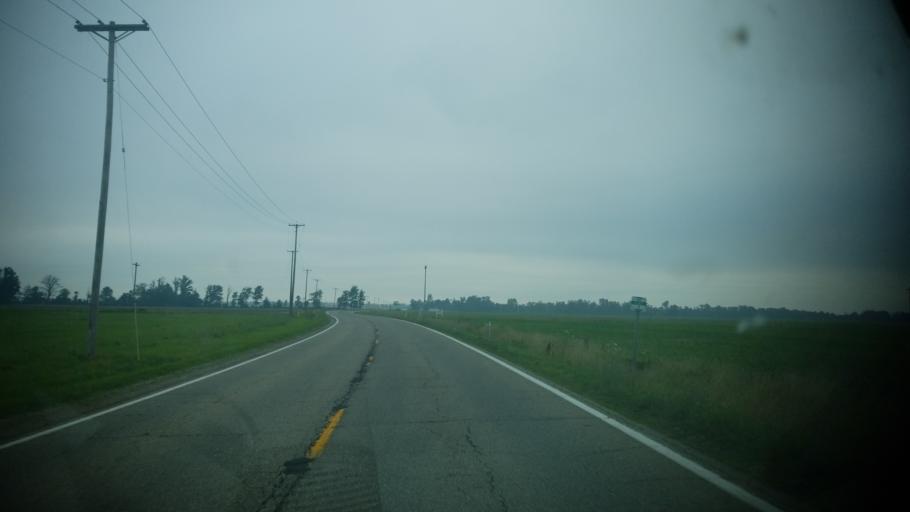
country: US
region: Illinois
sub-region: Clay County
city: Flora
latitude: 38.6464
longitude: -88.4380
